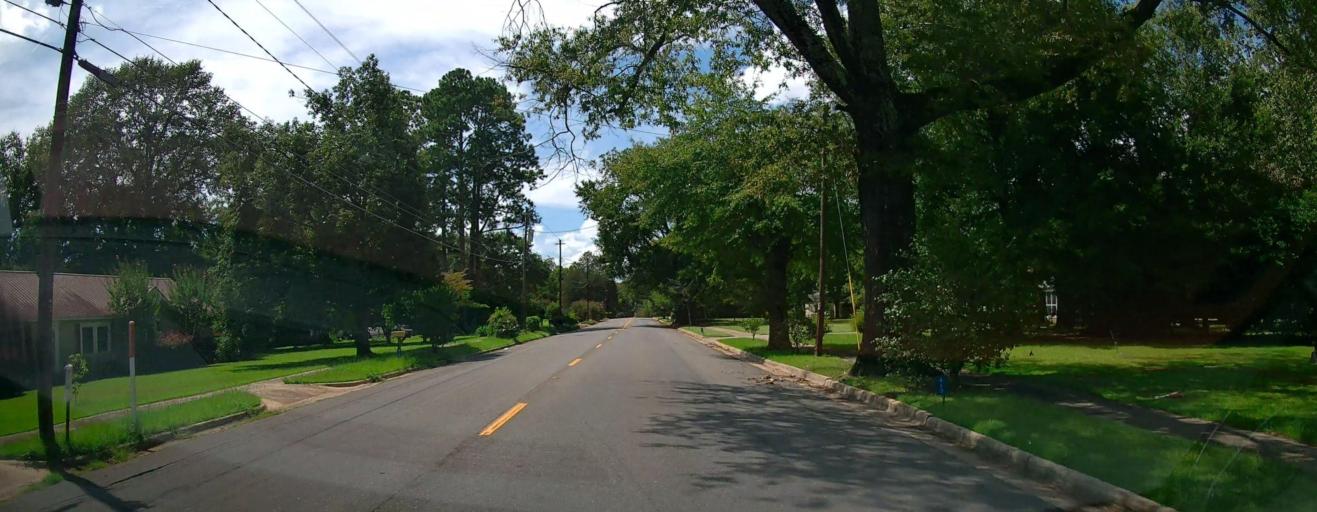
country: US
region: Georgia
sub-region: Macon County
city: Marshallville
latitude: 32.4564
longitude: -83.9509
